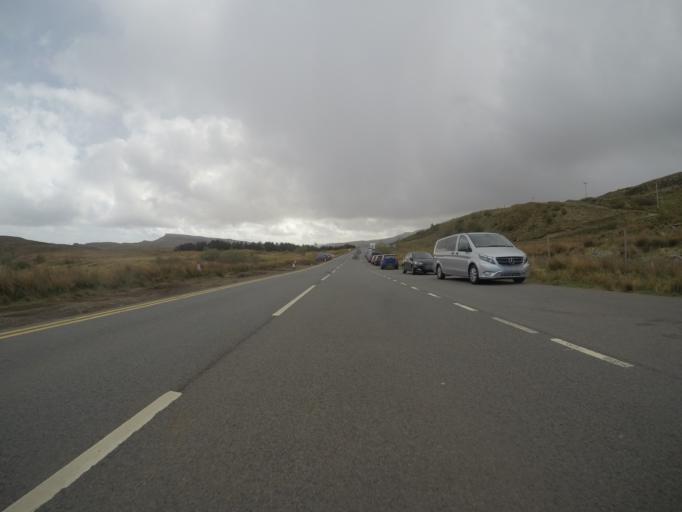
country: GB
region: Scotland
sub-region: Highland
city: Portree
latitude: 57.4989
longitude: -6.1577
